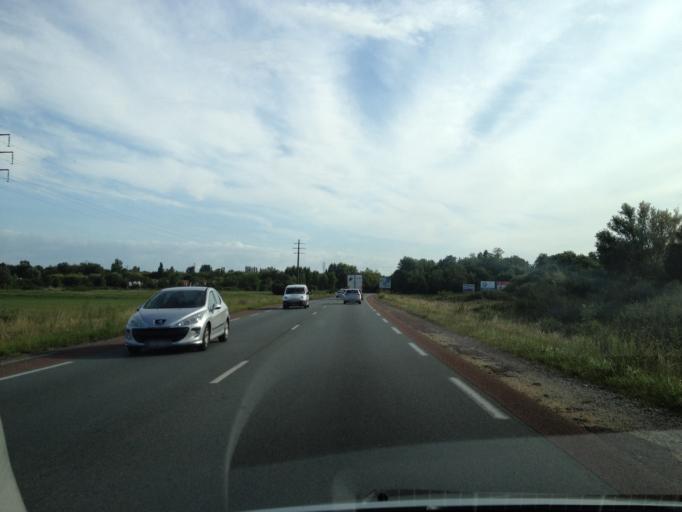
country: FR
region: Poitou-Charentes
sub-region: Departement de la Charente-Maritime
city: Rochefort
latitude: 45.9547
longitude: -0.9828
